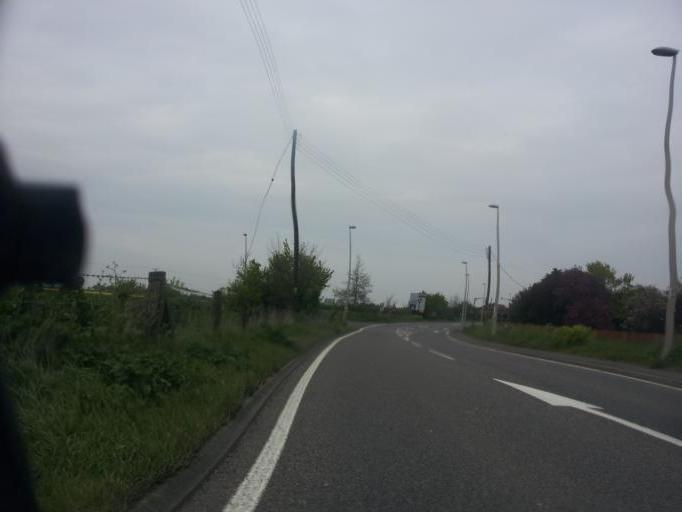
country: GB
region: England
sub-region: Medway
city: High Halstow
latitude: 51.4481
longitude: 0.5833
